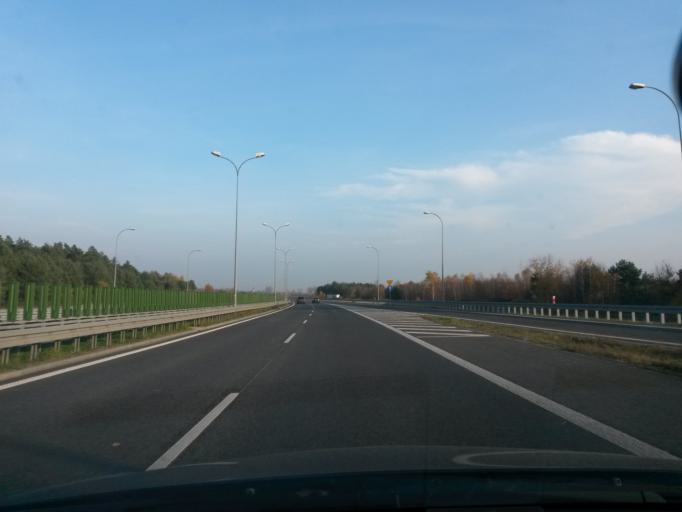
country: PL
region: Lower Silesian Voivodeship
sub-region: Powiat olesnicki
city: Olesnica
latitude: 51.2264
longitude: 17.4439
